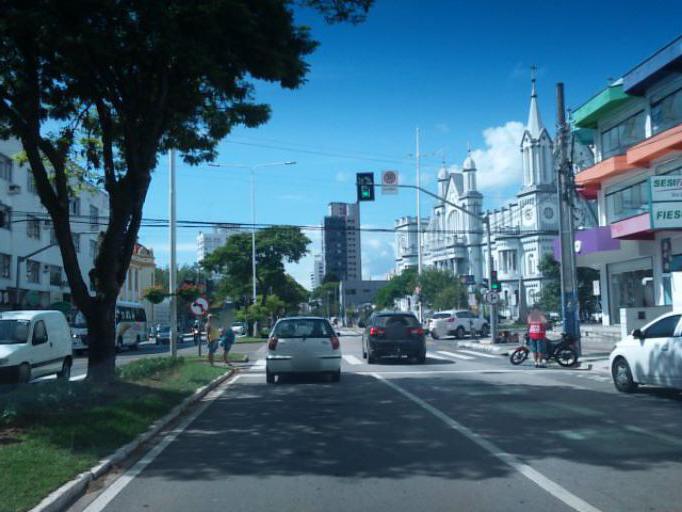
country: BR
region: Santa Catarina
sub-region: Itajai
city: Itajai
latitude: -26.9063
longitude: -48.6619
